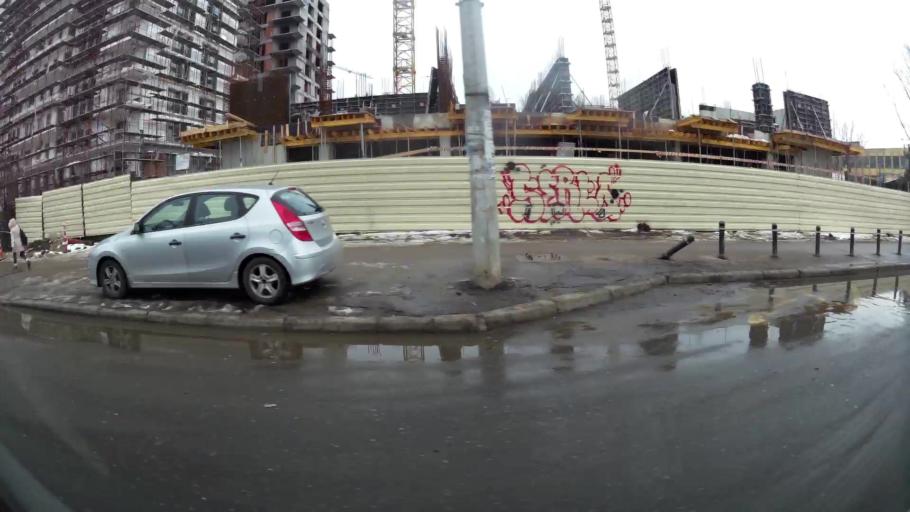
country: RO
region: Ilfov
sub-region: Comuna Chiajna
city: Rosu
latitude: 44.4147
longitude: 26.0351
